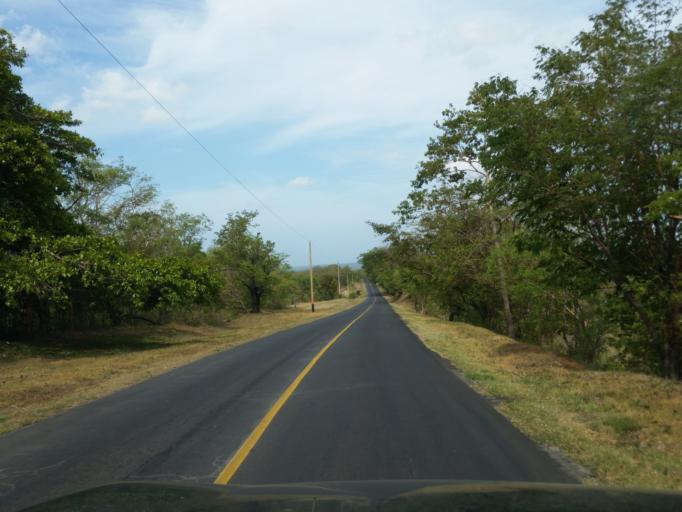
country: NI
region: Managua
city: San Rafael del Sur
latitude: 11.9014
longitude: -86.3879
